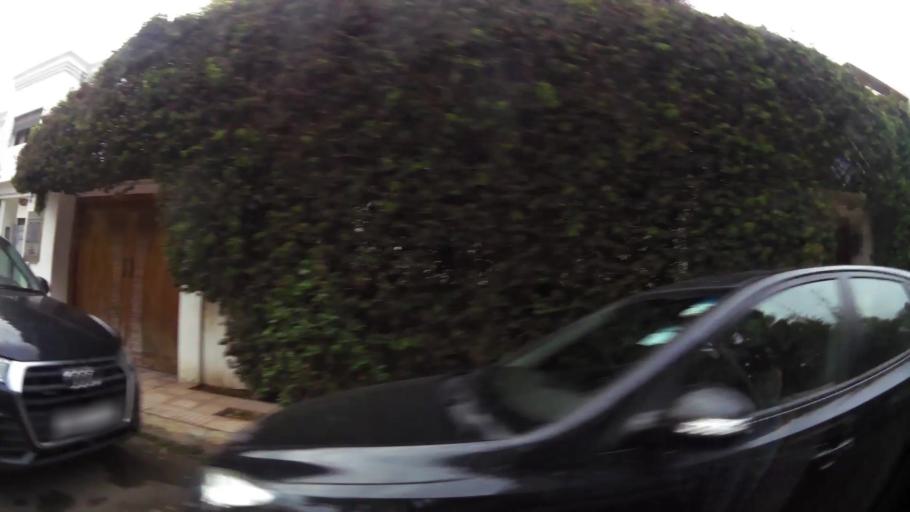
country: MA
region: Grand Casablanca
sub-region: Casablanca
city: Casablanca
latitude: 33.5797
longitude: -7.6766
